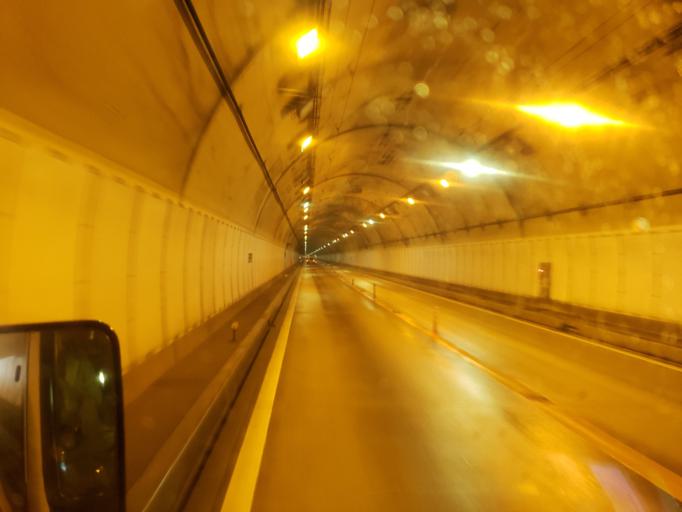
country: JP
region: Hyogo
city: Nishiwaki
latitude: 35.1516
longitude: 134.7865
